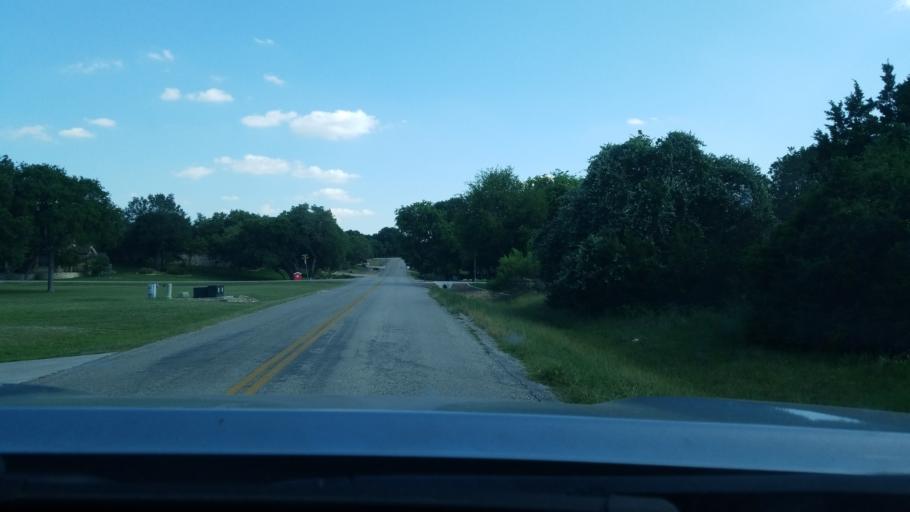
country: US
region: Texas
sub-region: Comal County
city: Bulverde
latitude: 29.8244
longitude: -98.3998
